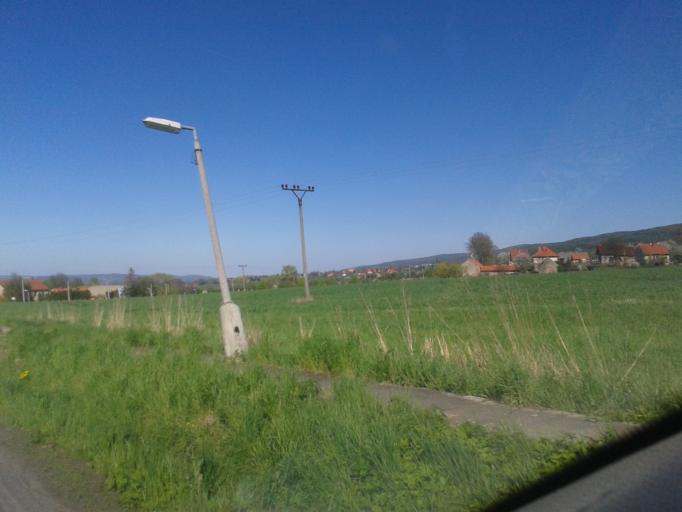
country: CZ
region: Central Bohemia
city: Dobris
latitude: 49.8731
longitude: 14.1417
